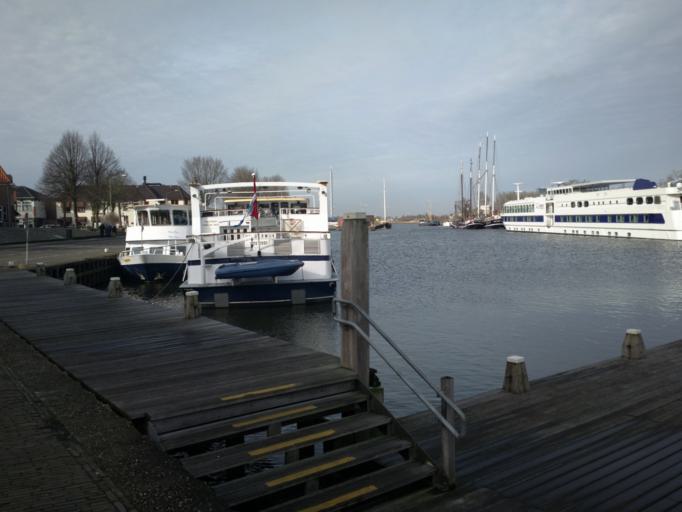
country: NL
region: Gelderland
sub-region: Gemeente Harderwijk
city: Harderwijk
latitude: 52.3521
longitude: 5.6227
